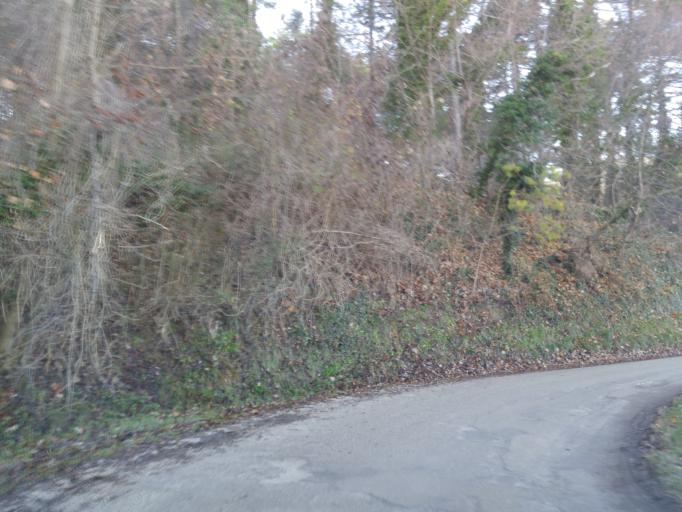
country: IT
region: The Marches
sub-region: Provincia di Pesaro e Urbino
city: Fossombrone
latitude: 43.6988
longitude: 12.7944
